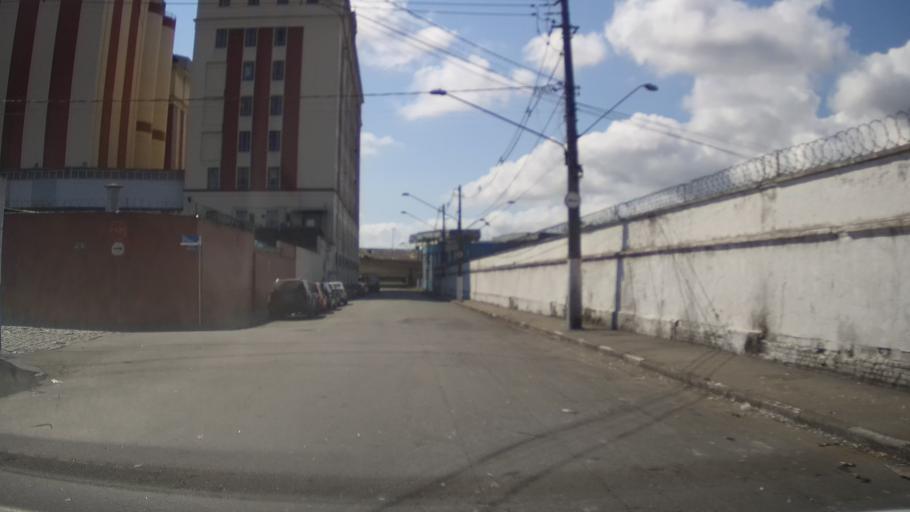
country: BR
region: Sao Paulo
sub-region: Santos
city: Santos
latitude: -23.9380
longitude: -46.3175
